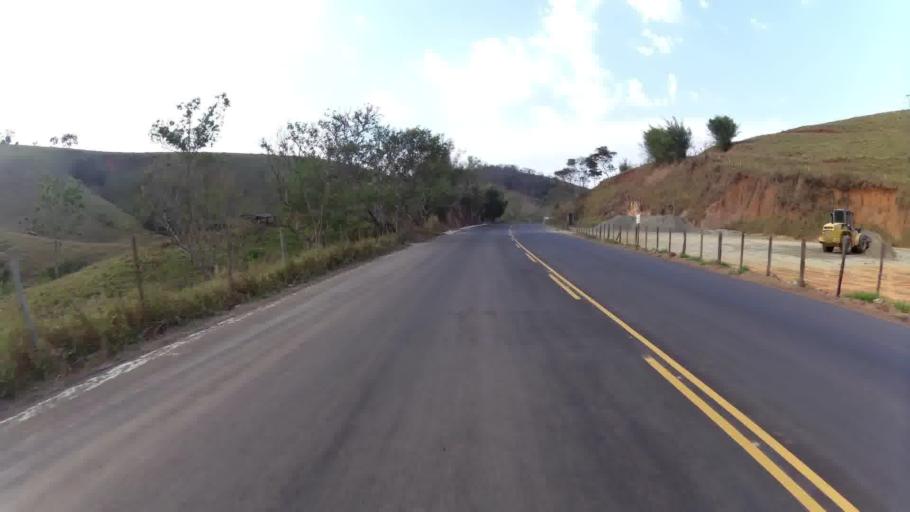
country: BR
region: Rio de Janeiro
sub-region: Santo Antonio De Padua
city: Santo Antonio de Padua
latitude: -21.4938
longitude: -42.0732
